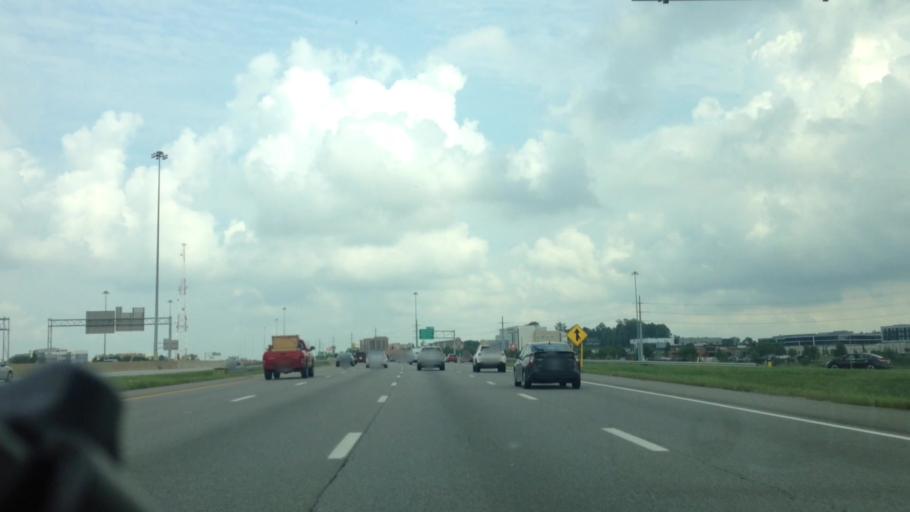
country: US
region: Ohio
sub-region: Cuyahoga County
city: Orange
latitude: 41.4478
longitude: -81.4917
